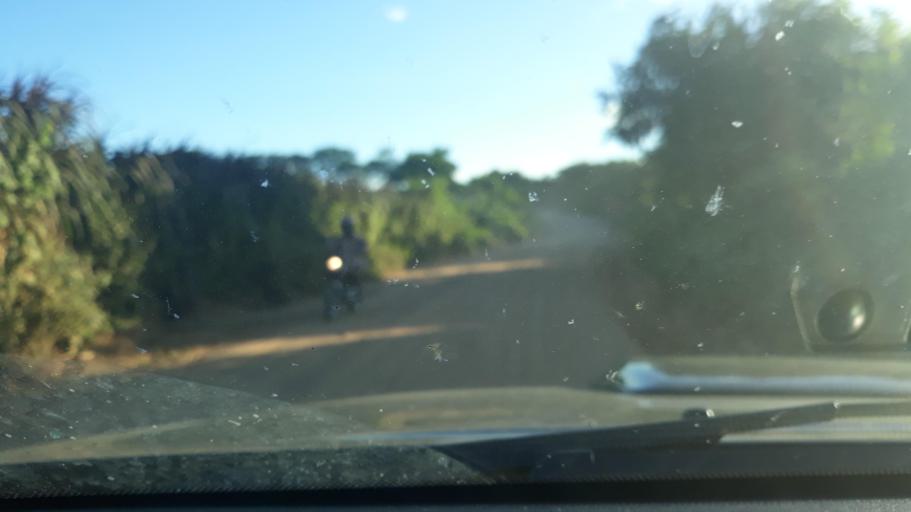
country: BR
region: Bahia
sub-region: Riacho De Santana
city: Riacho de Santana
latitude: -13.7975
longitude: -42.7122
